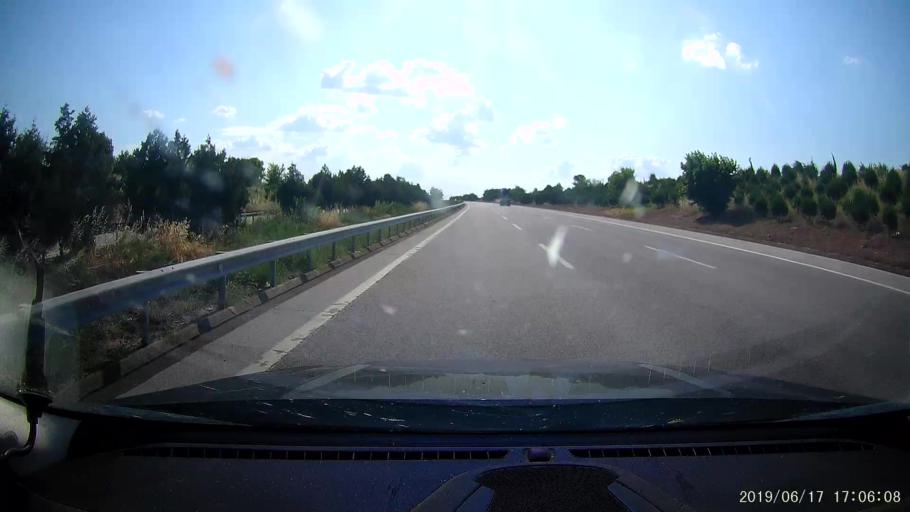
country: TR
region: Edirne
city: Edirne
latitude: 41.6624
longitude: 26.6795
